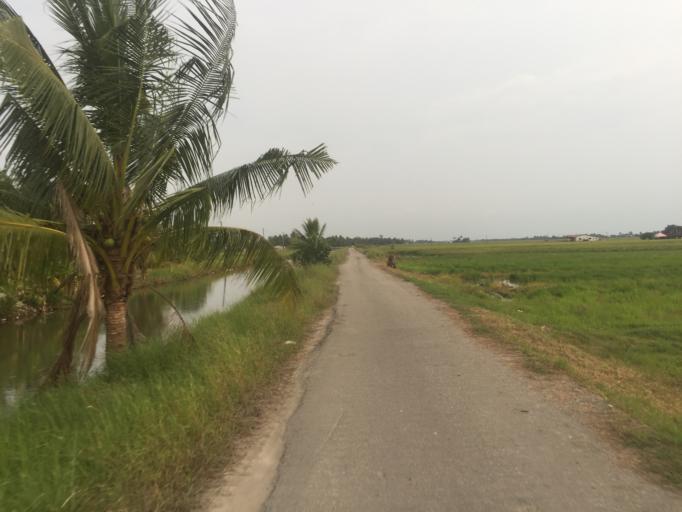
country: MY
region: Kedah
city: Kuala Kedah
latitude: 6.0834
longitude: 100.3113
